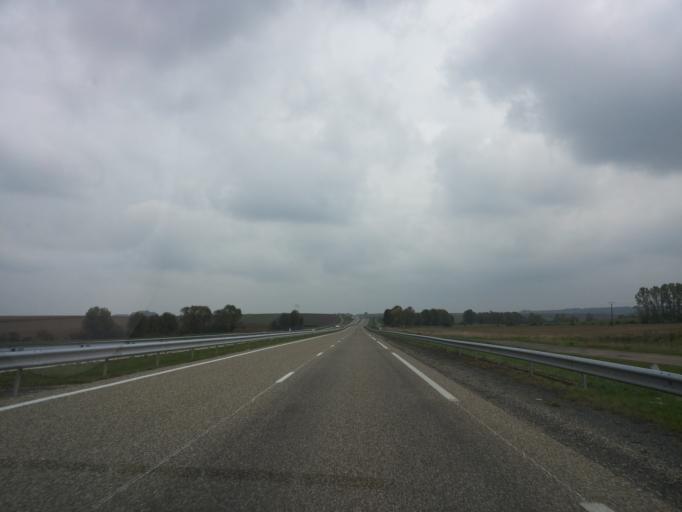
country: FR
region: Lorraine
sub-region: Departement de la Moselle
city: Dieuze
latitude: 48.7368
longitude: 6.6768
